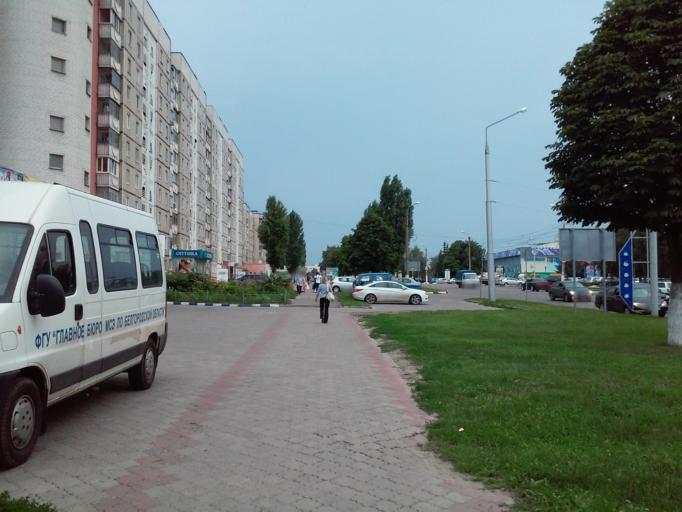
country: RU
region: Belgorod
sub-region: Belgorodskiy Rayon
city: Belgorod
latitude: 50.5730
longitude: 36.5828
